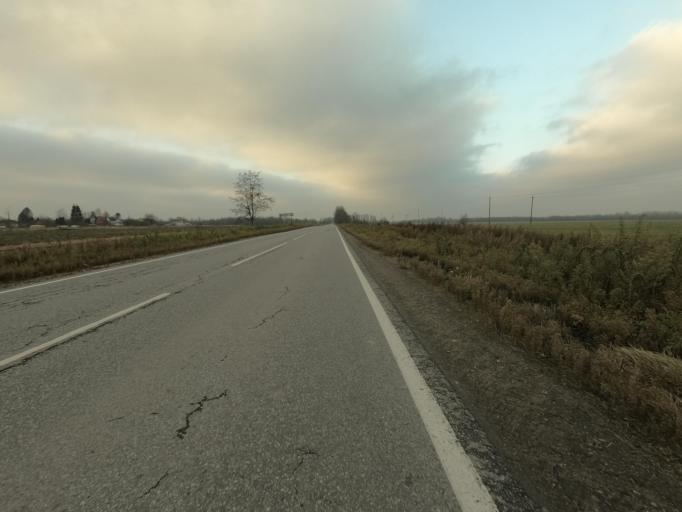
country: RU
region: Leningrad
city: Mga
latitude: 59.7644
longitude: 31.0173
